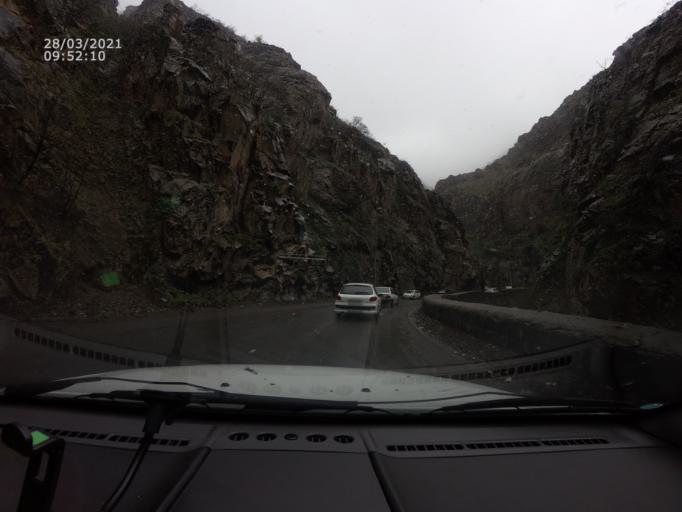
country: IR
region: Mazandaran
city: Chalus
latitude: 36.2922
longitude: 51.2455
